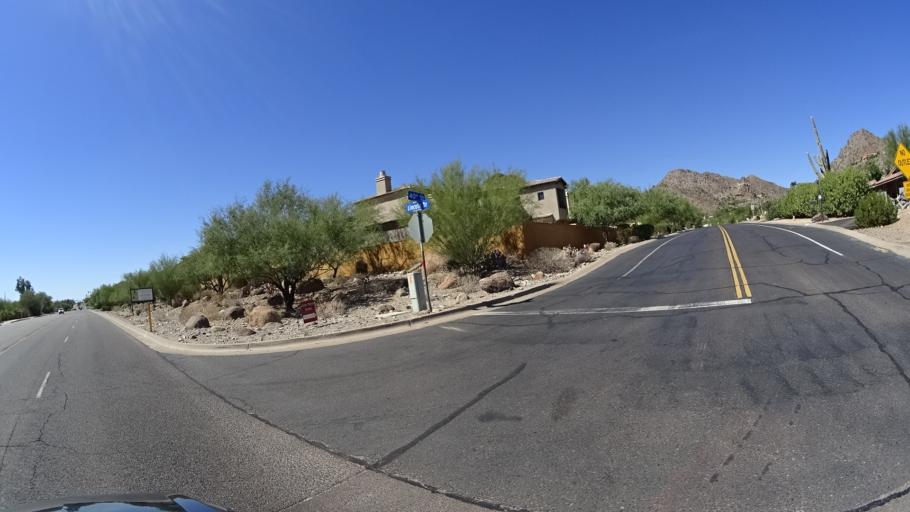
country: US
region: Arizona
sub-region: Maricopa County
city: Paradise Valley
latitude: 33.5319
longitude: -111.9950
